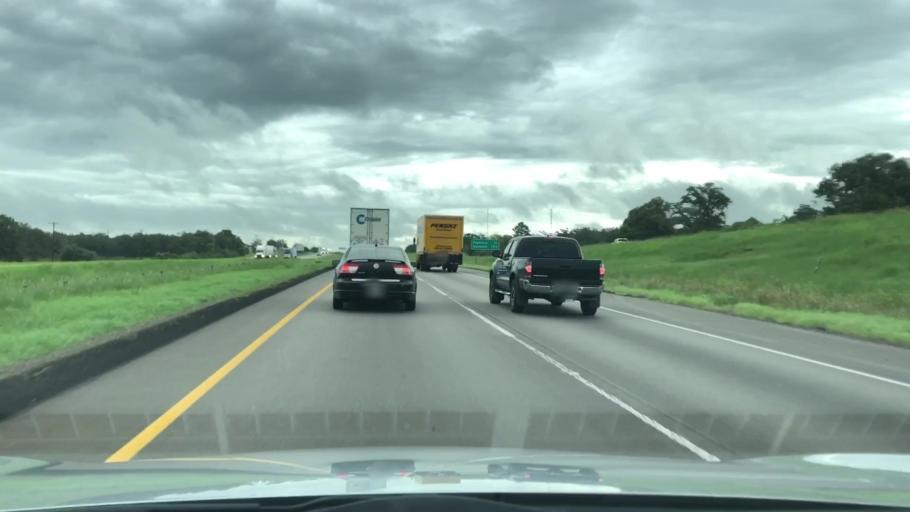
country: US
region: Texas
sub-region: Caldwell County
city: Luling
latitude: 29.6541
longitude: -97.5774
